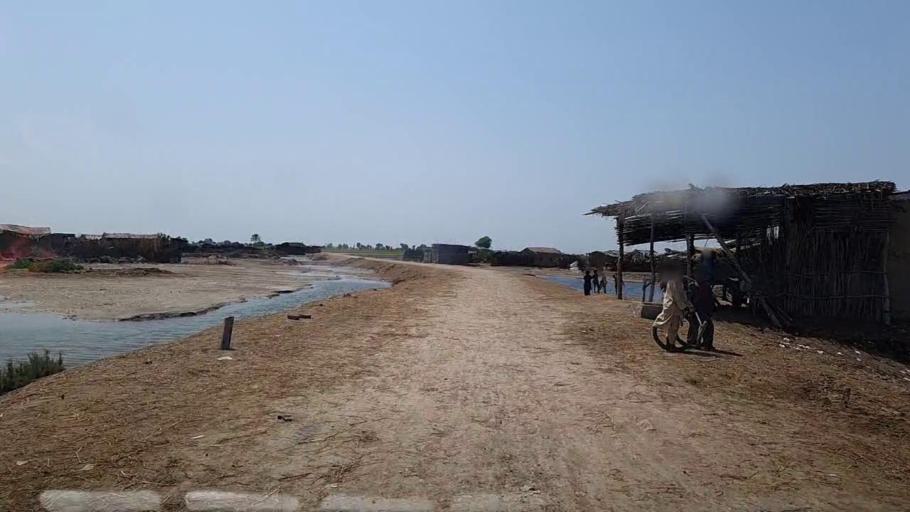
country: PK
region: Sindh
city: Kario
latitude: 24.6358
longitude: 68.4900
